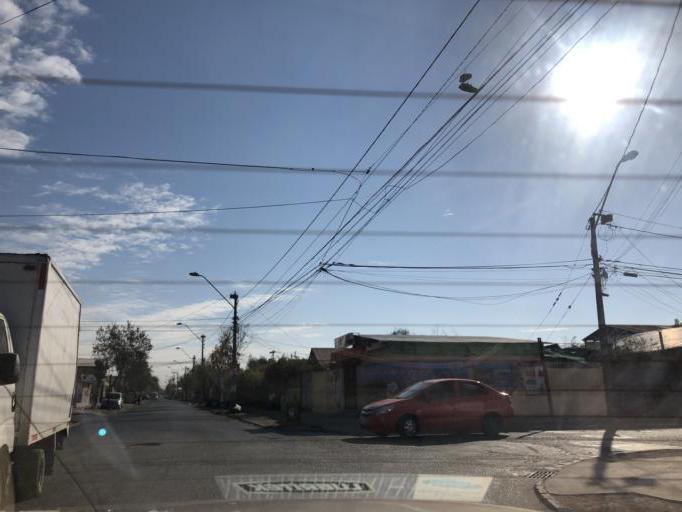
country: CL
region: Santiago Metropolitan
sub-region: Provincia de Cordillera
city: Puente Alto
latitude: -33.6228
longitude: -70.5915
